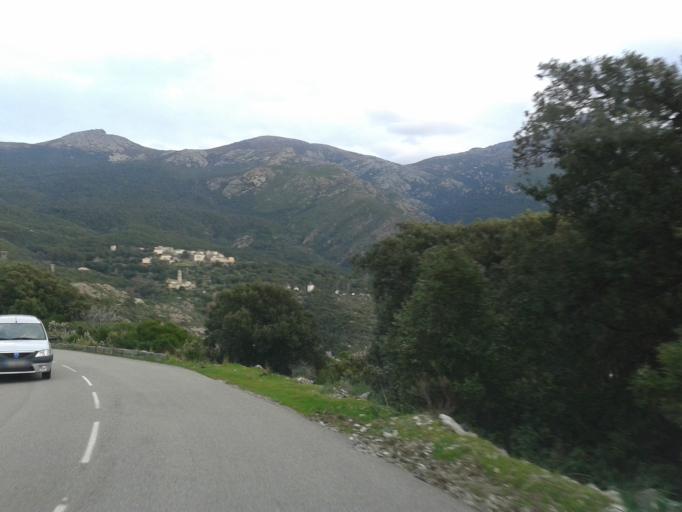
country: FR
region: Corsica
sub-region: Departement de la Haute-Corse
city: Brando
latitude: 42.8698
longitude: 9.3426
